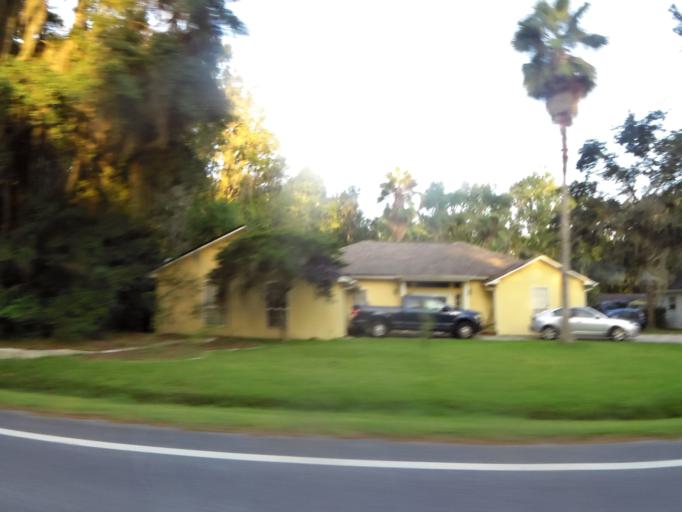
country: US
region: Florida
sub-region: Saint Johns County
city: Fruit Cove
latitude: 30.1803
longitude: -81.6381
